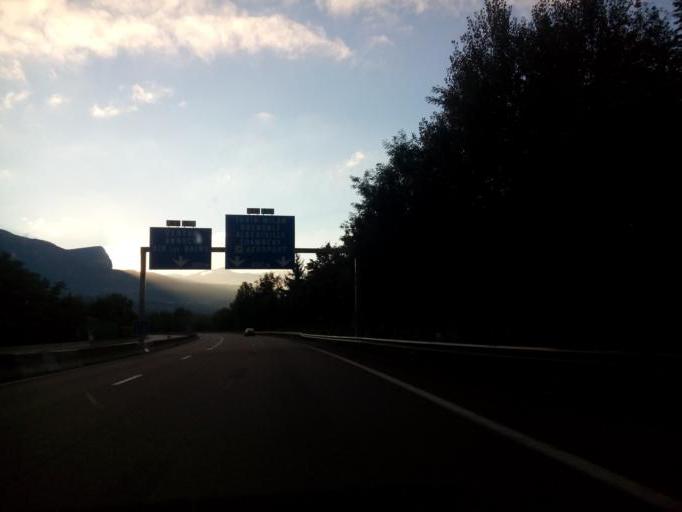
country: FR
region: Rhone-Alpes
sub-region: Departement de la Savoie
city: La Motte-Servolex
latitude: 45.6035
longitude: 5.8709
